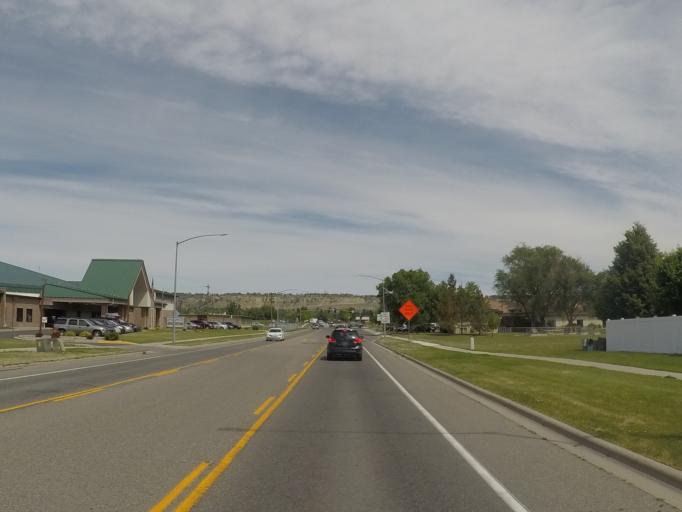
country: US
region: Montana
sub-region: Yellowstone County
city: Billings
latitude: 45.7748
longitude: -108.5969
